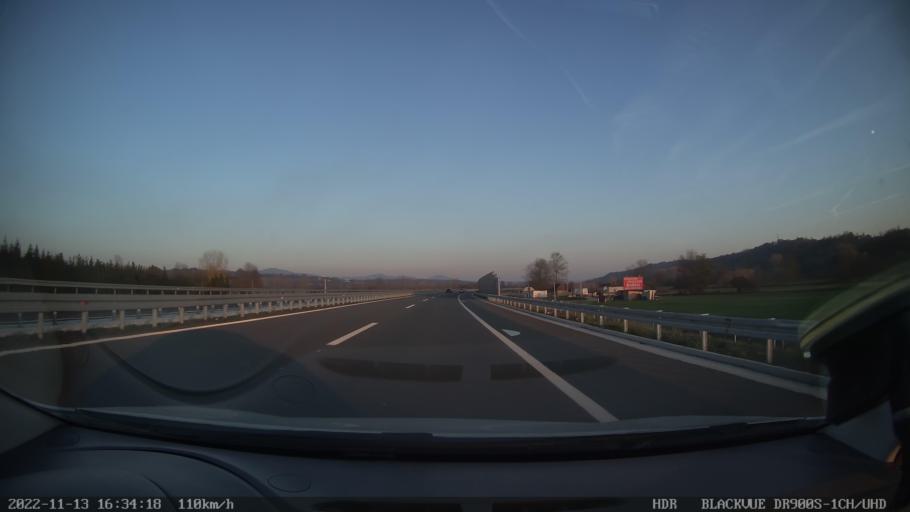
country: RS
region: Central Serbia
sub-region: Moravicki Okrug
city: Cacak
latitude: 43.9295
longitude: 20.3304
